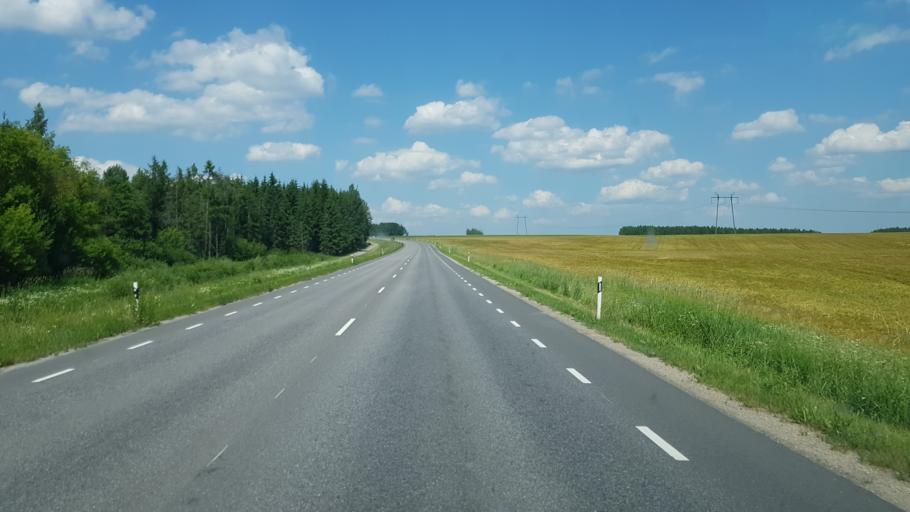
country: EE
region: Tartu
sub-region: Tartu linn
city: Tartu
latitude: 58.4694
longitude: 26.6795
